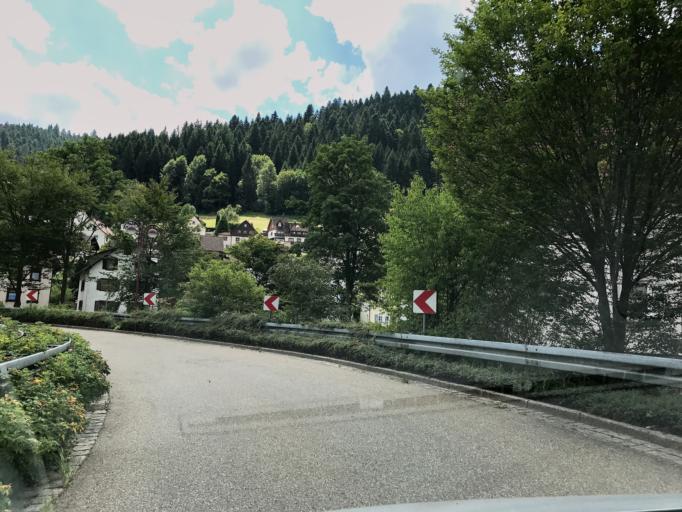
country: DE
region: Baden-Wuerttemberg
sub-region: Freiburg Region
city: Schiltach
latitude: 48.2871
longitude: 8.3419
